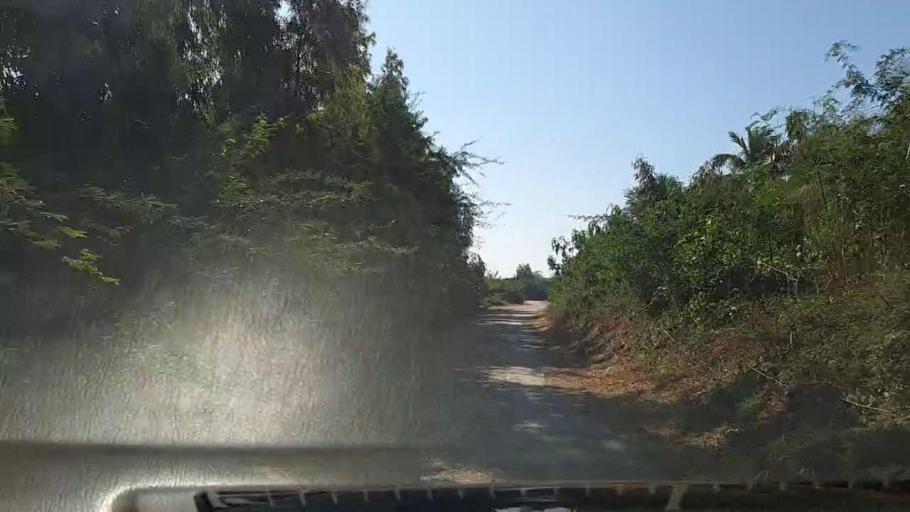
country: PK
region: Sindh
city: Thatta
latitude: 24.7105
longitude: 67.9189
